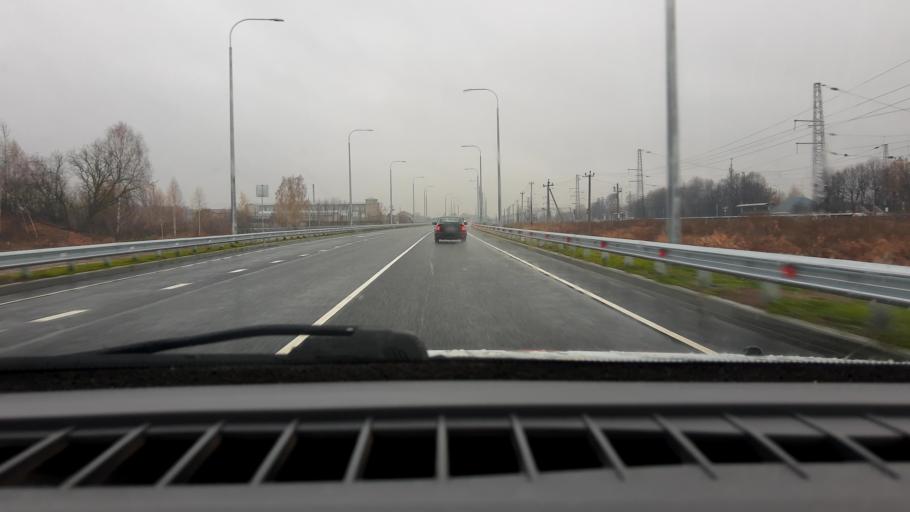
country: RU
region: Nizjnij Novgorod
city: Neklyudovo
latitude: 56.4094
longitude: 43.9833
